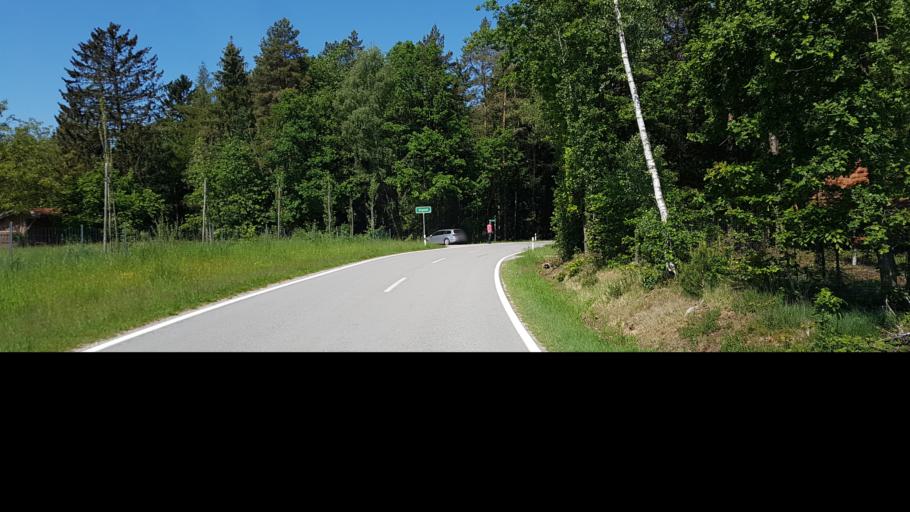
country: DE
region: Bavaria
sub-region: Lower Bavaria
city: Simbach am Inn
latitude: 48.3001
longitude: 13.0381
